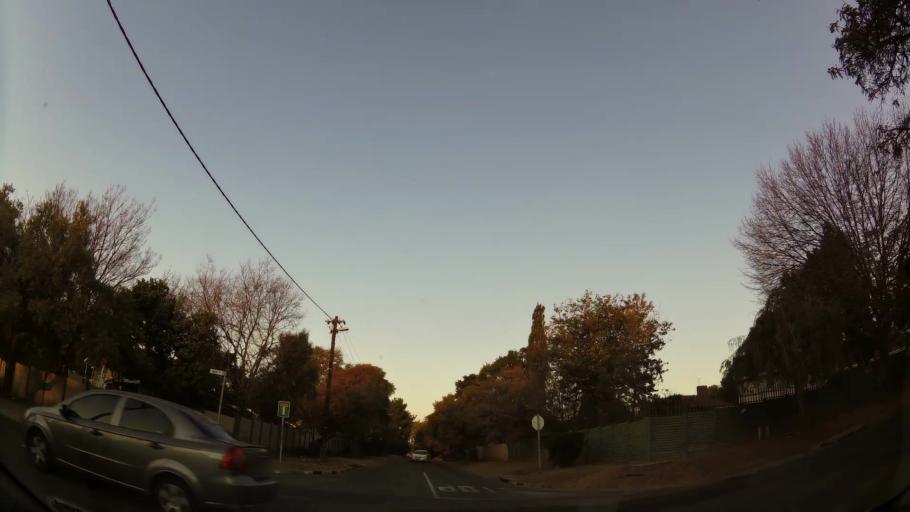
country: ZA
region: Gauteng
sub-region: City of Johannesburg Metropolitan Municipality
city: Johannesburg
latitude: -26.1217
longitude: 27.9947
